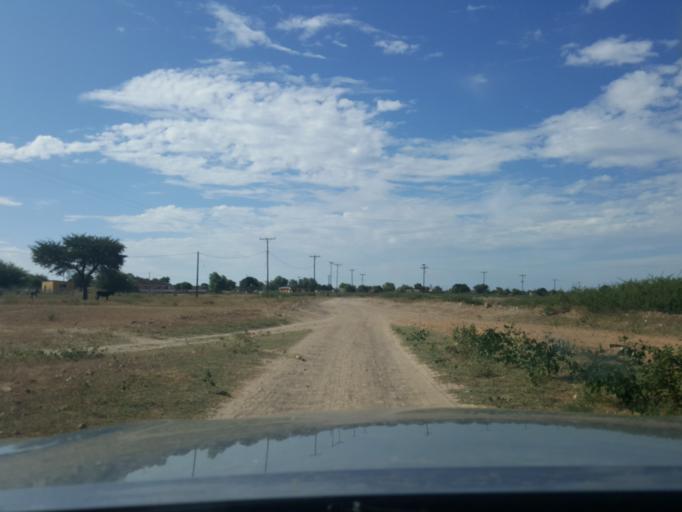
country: BW
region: Kweneng
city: Khudumelapye
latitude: -23.6938
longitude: 24.7170
